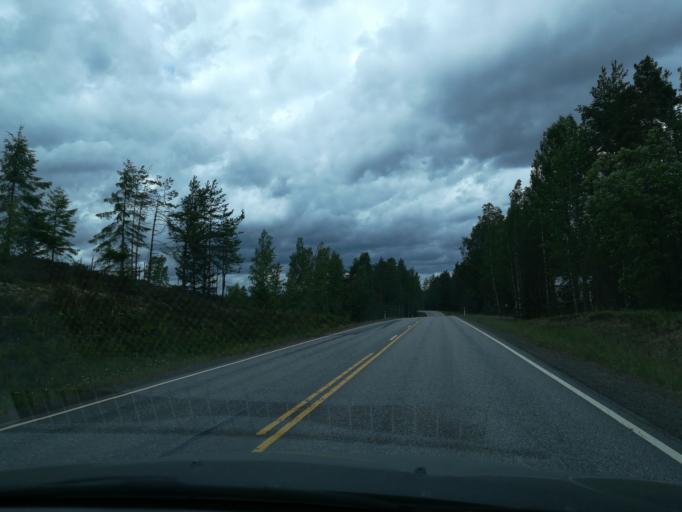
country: FI
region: South Karelia
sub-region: Lappeenranta
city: Taipalsaari
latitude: 61.0909
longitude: 27.9434
